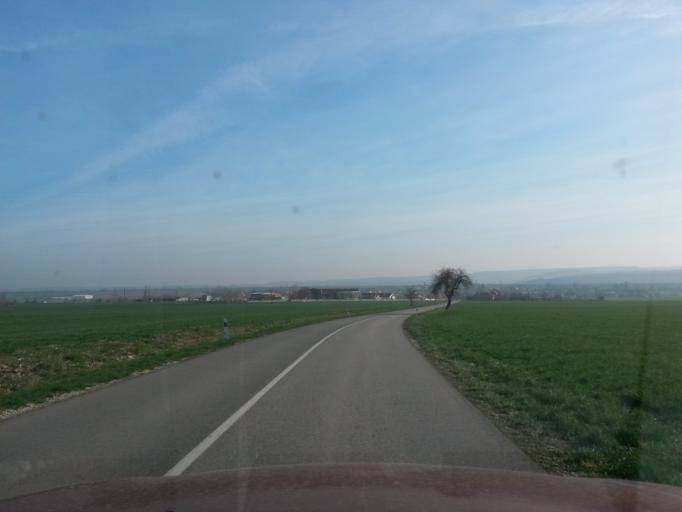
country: SK
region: Nitriansky
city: Svodin
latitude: 47.9807
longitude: 18.3880
